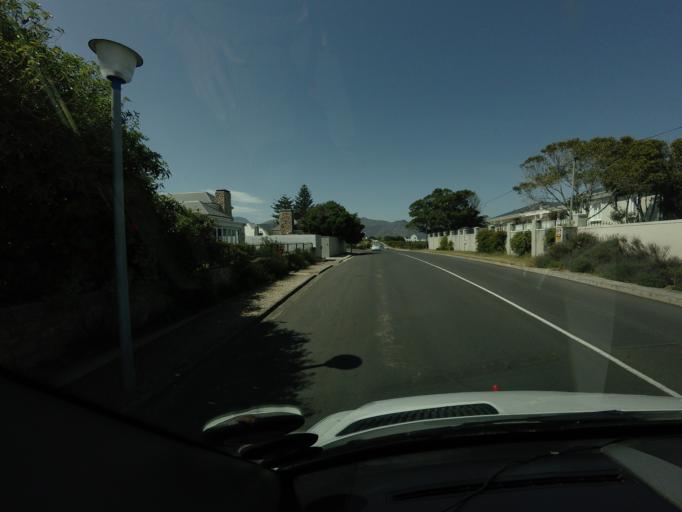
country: ZA
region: Western Cape
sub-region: Overberg District Municipality
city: Hermanus
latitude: -34.4275
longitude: 19.2290
